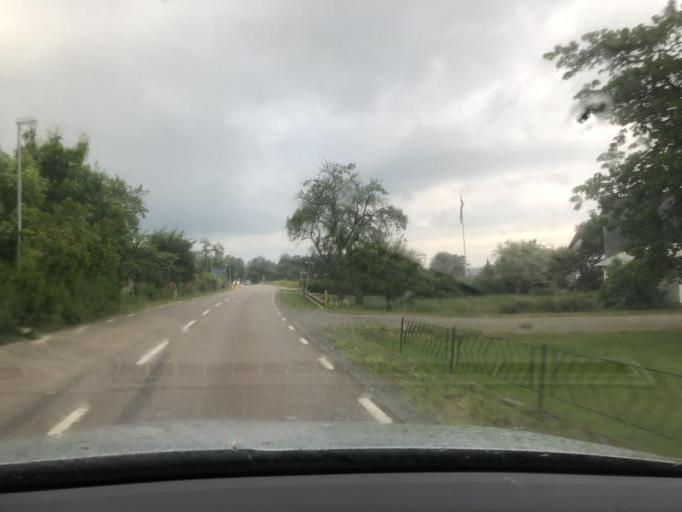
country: SE
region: Blekinge
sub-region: Solvesborgs Kommun
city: Soelvesborg
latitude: 56.1004
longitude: 14.6172
